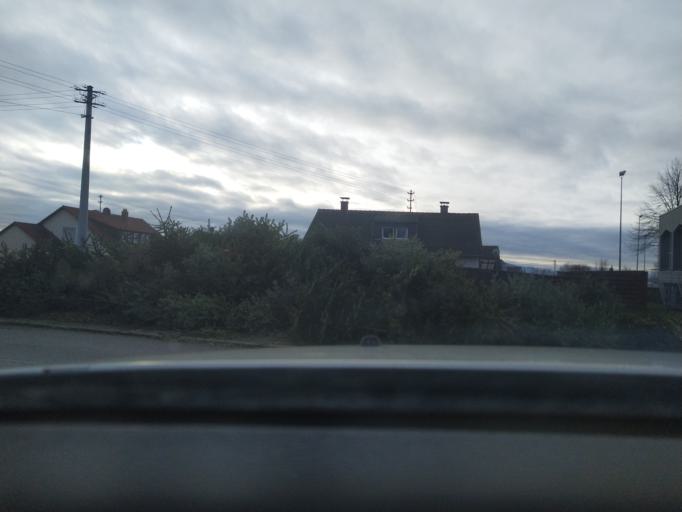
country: DE
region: Baden-Wuerttemberg
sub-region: Regierungsbezirk Stuttgart
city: Durlangen
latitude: 48.8597
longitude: 9.7889
